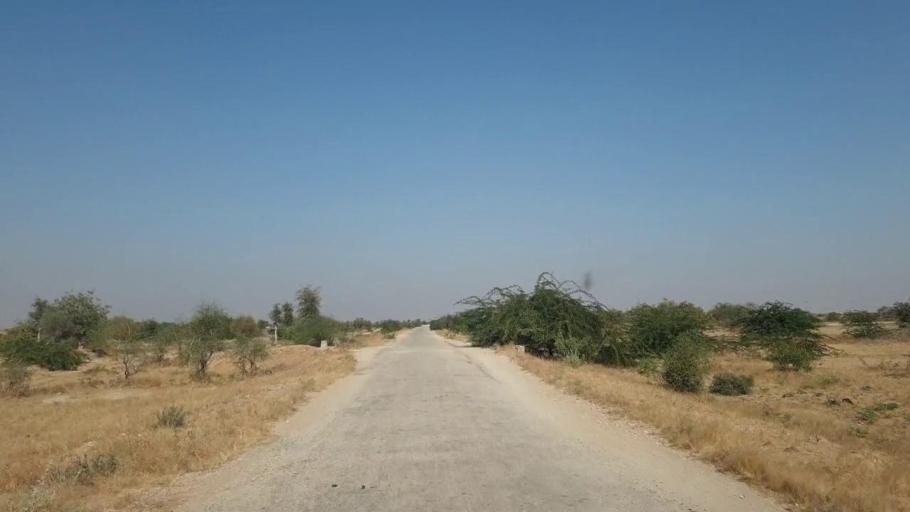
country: PK
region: Sindh
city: Jamshoro
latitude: 25.3796
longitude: 67.8437
